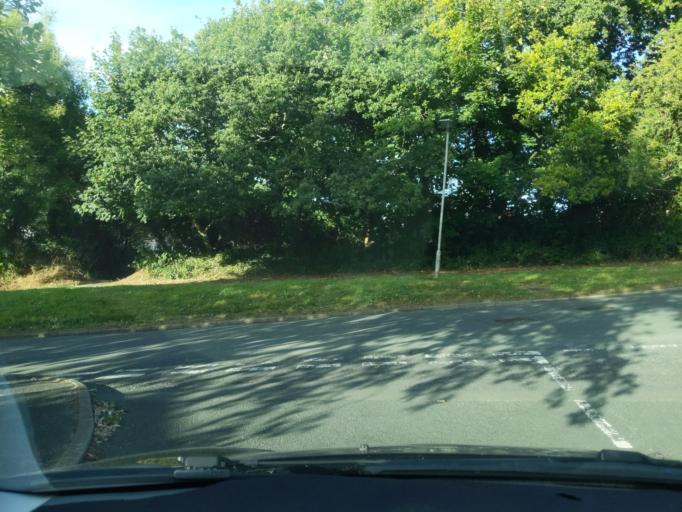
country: GB
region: England
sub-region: Plymouth
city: Plymstock
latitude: 50.3935
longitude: -4.1056
